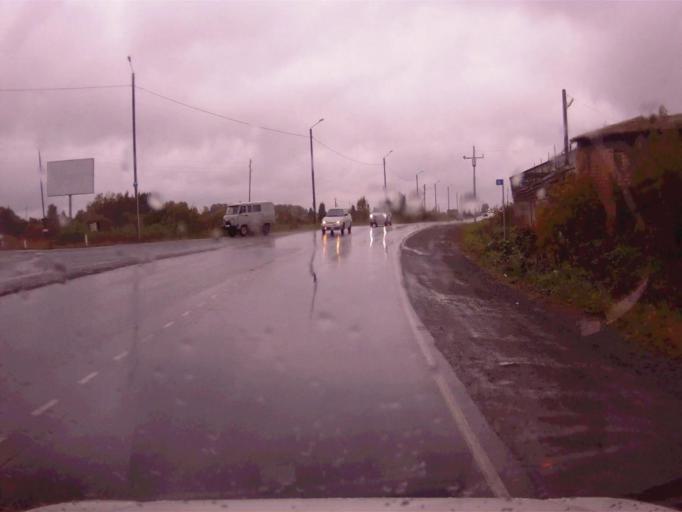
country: RU
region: Chelyabinsk
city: Argayash
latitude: 55.4773
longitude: 60.8655
